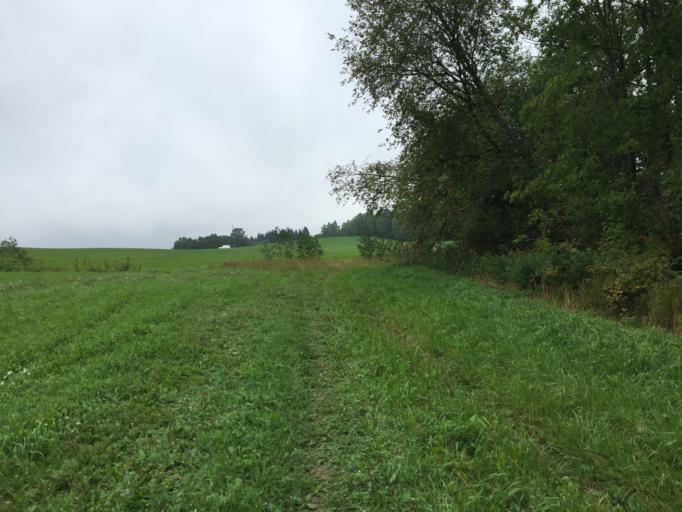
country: NO
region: Akershus
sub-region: Baerum
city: Lysaker
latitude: 59.9826
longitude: 10.6197
